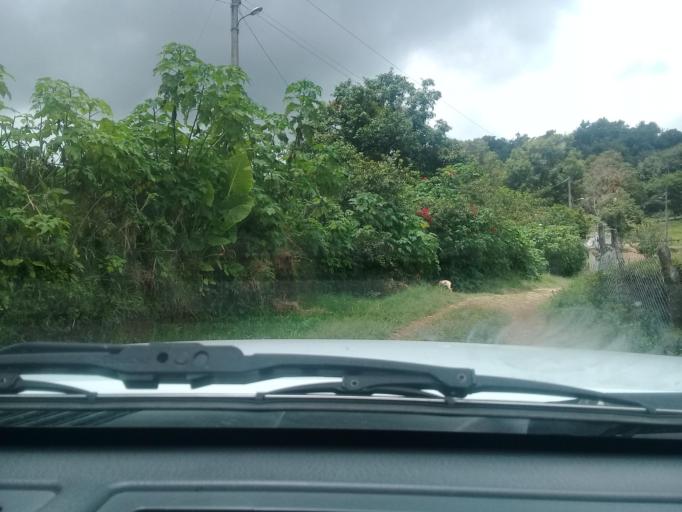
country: MX
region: Veracruz
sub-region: Tlalnelhuayocan
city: Otilpan
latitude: 19.5473
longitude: -96.9763
